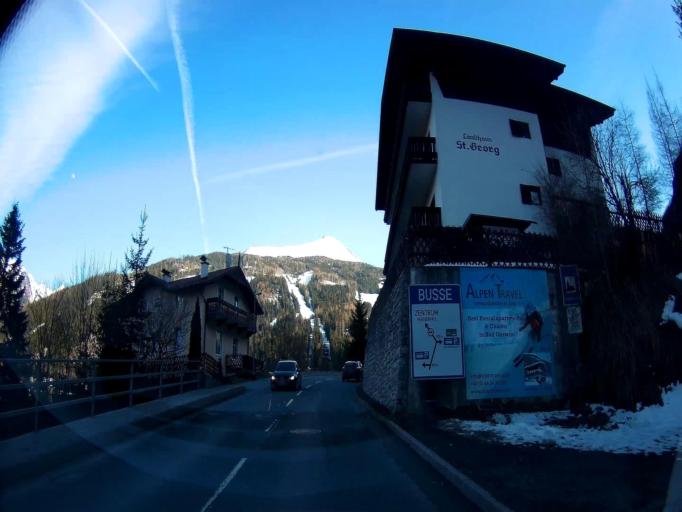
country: AT
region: Salzburg
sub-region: Politischer Bezirk Sankt Johann im Pongau
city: Bad Gastein
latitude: 47.1208
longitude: 13.1324
